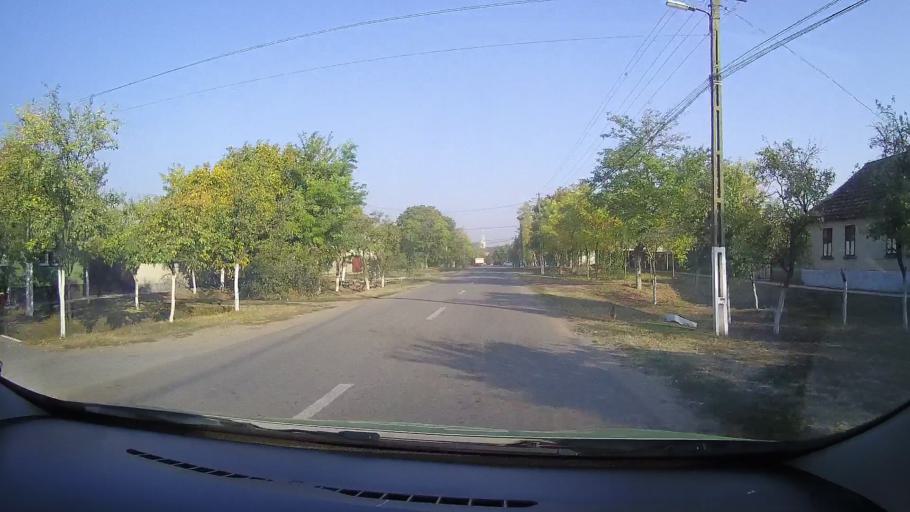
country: RO
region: Arad
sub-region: Comuna Graniceri
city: Graniceri
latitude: 46.5157
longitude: 21.3052
